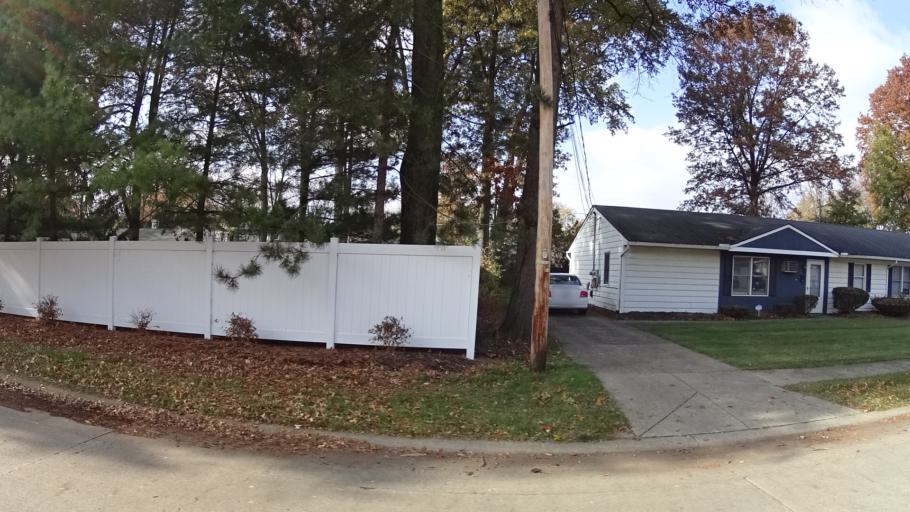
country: US
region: Ohio
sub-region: Lorain County
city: Elyria
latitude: 41.3670
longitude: -82.0805
